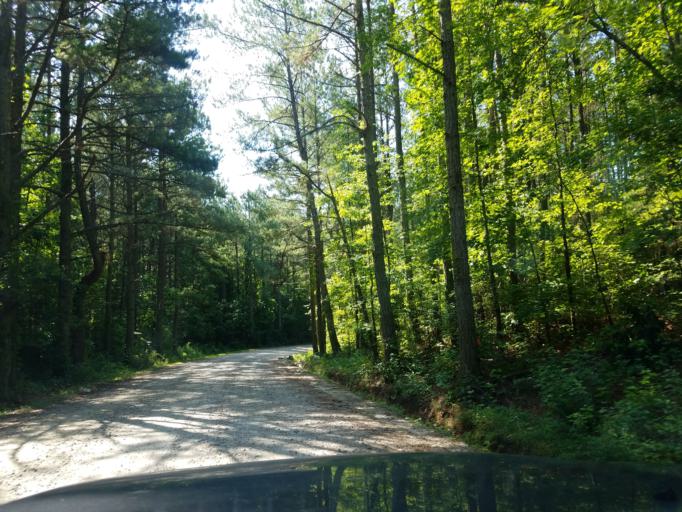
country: US
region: North Carolina
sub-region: Vance County
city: Henderson
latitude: 36.3424
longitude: -78.4203
